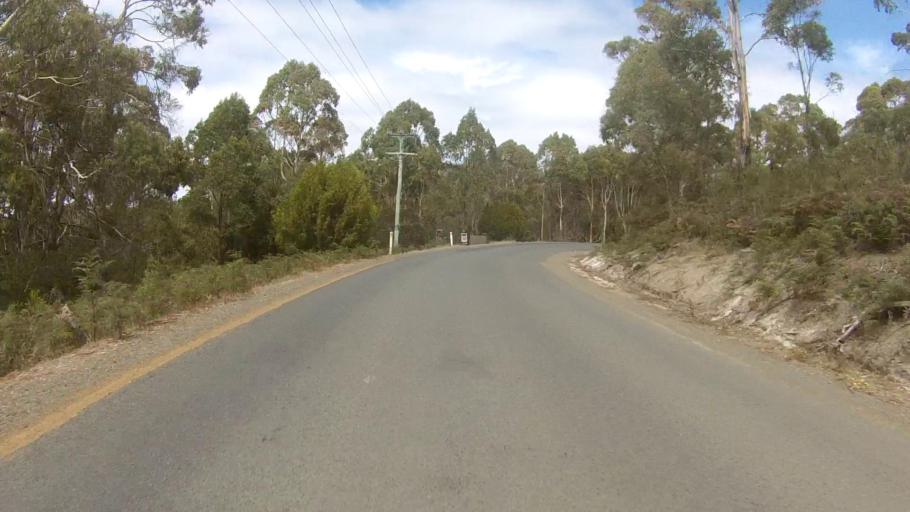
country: AU
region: Tasmania
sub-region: Kingborough
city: Blackmans Bay
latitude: -43.0147
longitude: 147.3235
